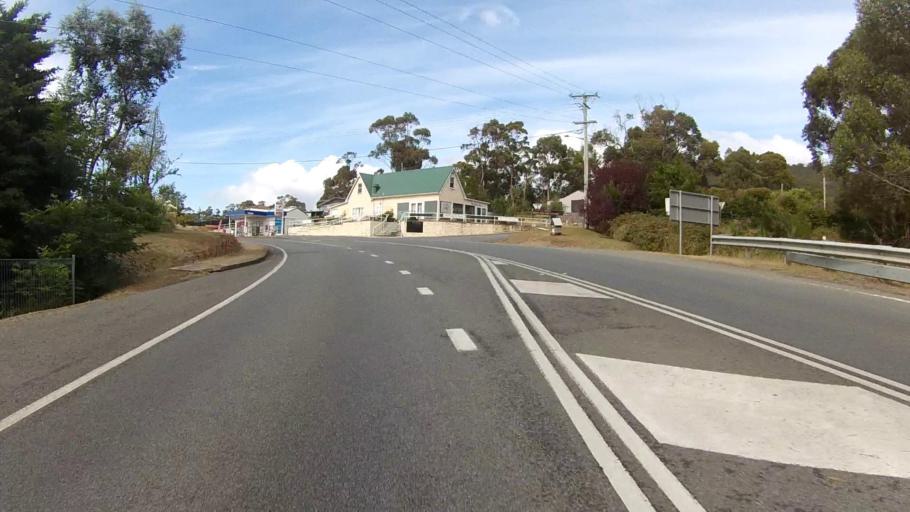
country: AU
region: Tasmania
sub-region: Kingborough
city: Kettering
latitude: -43.1226
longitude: 147.2454
